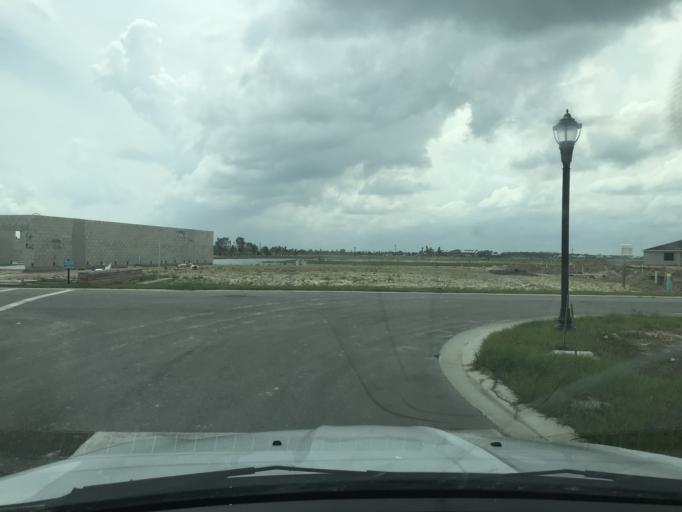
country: US
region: Florida
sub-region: Lee County
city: Olga
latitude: 26.7866
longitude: -81.7357
